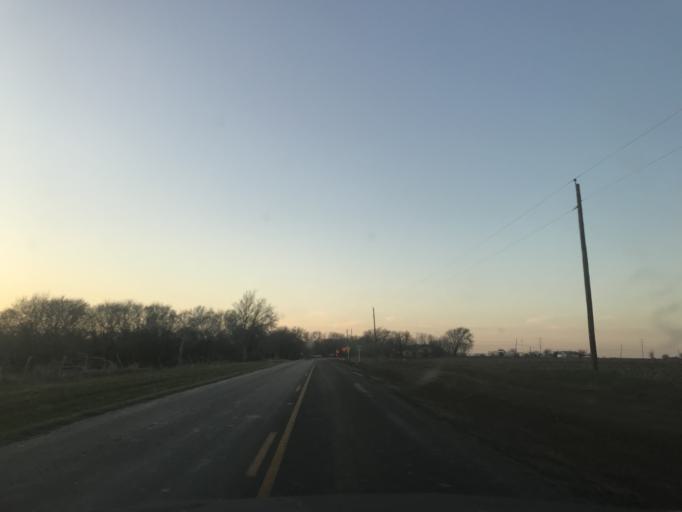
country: US
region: Texas
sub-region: Williamson County
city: Hutto
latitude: 30.5036
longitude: -97.5177
